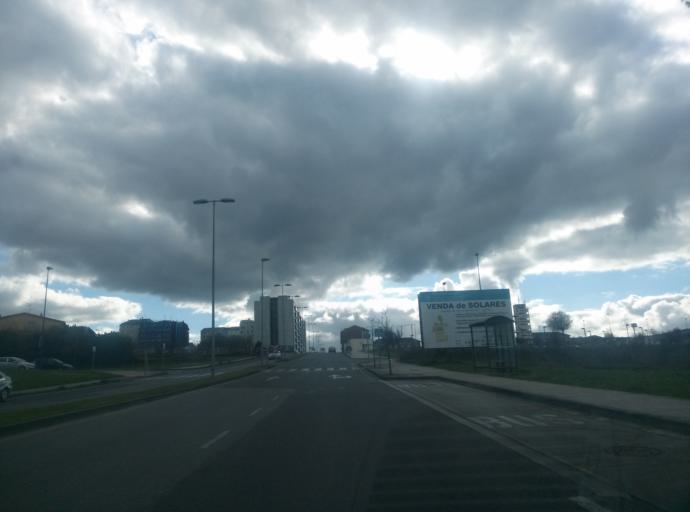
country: ES
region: Galicia
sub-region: Provincia de Lugo
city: Lugo
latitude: 43.0334
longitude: -7.5680
